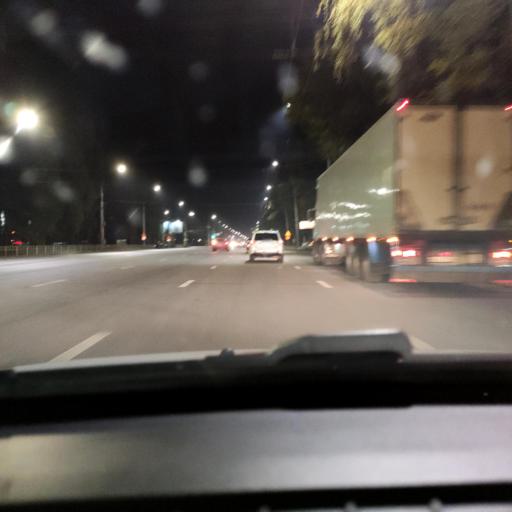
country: RU
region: Voronezj
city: Voronezh
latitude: 51.6315
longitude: 39.2317
